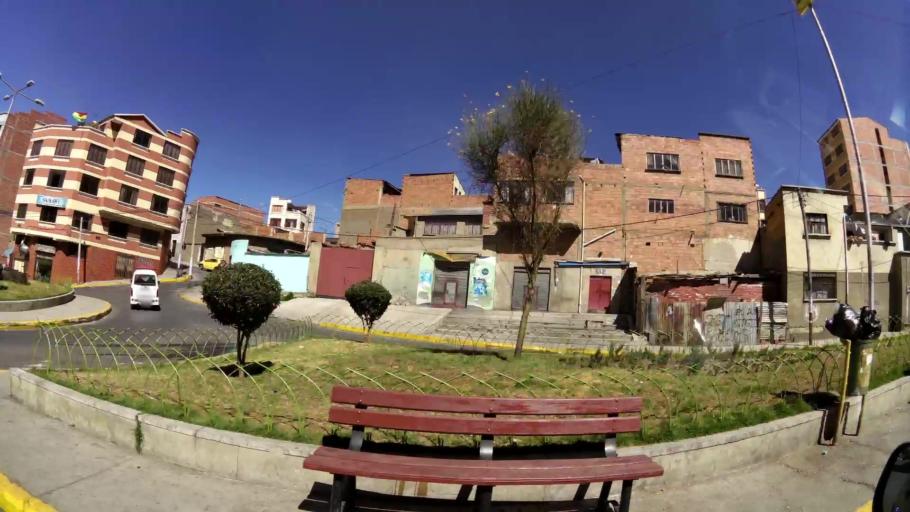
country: BO
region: La Paz
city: La Paz
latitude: -16.4931
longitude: -68.1510
